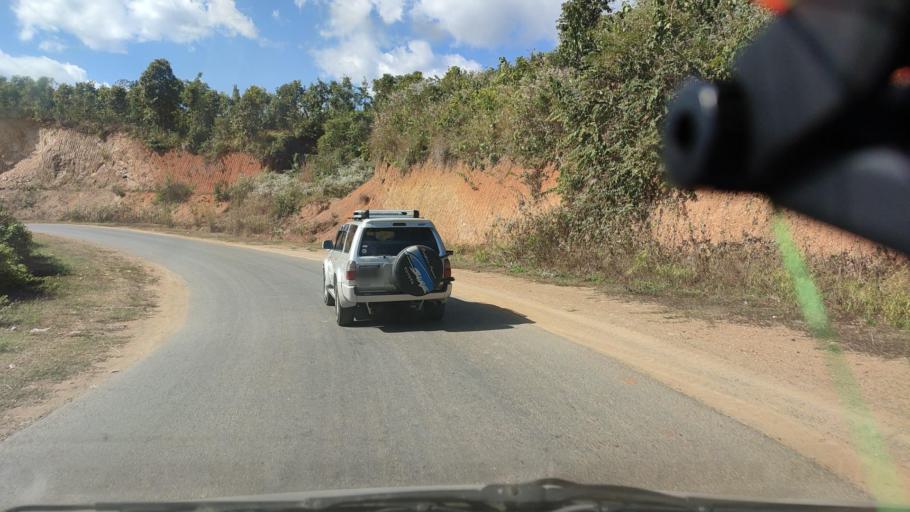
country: MM
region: Shan
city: Taunggyi
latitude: 21.2561
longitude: 97.6545
